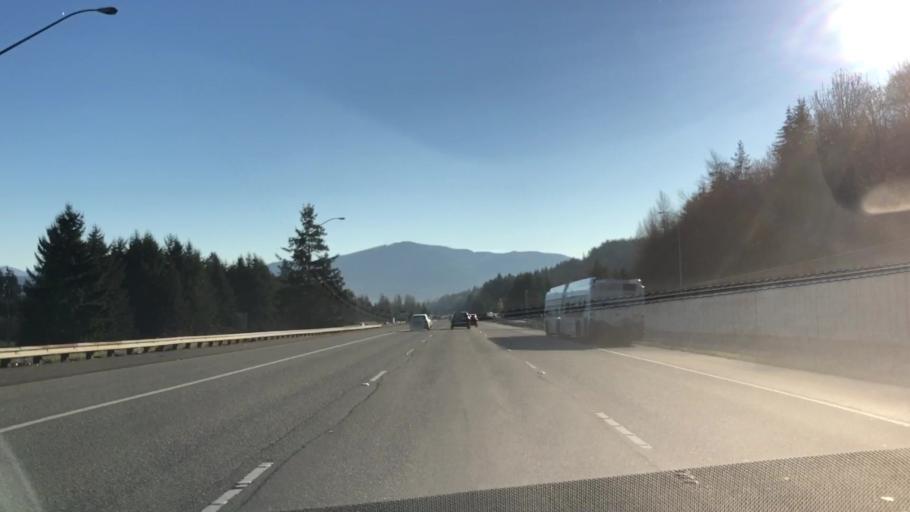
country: US
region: Washington
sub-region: King County
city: West Lake Sammamish
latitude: 47.5676
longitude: -122.1040
